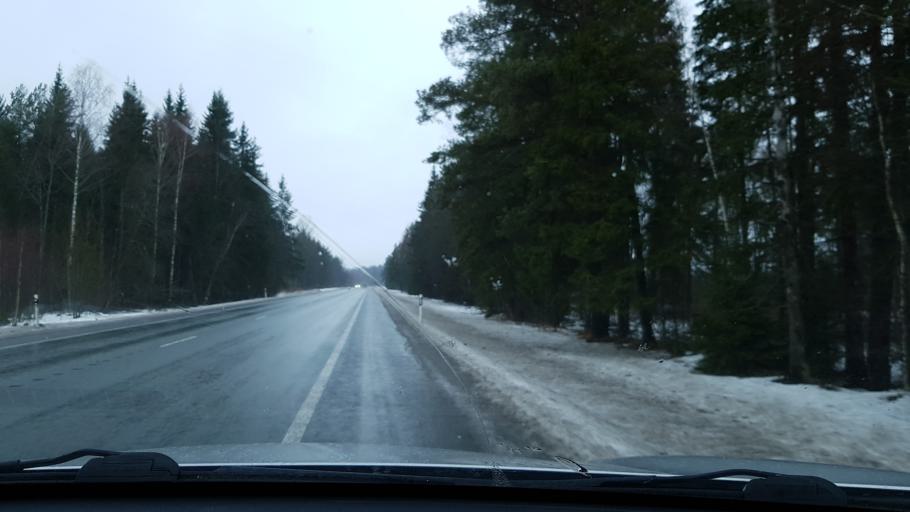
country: EE
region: Raplamaa
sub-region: Kohila vald
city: Kohila
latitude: 59.1563
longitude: 24.7771
